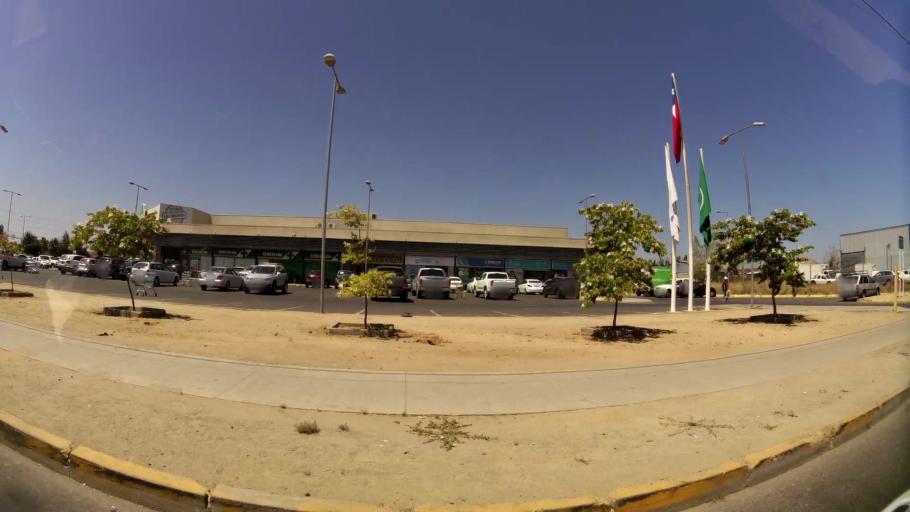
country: CL
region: Maule
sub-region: Provincia de Talca
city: Talca
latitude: -35.4321
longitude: -71.6282
